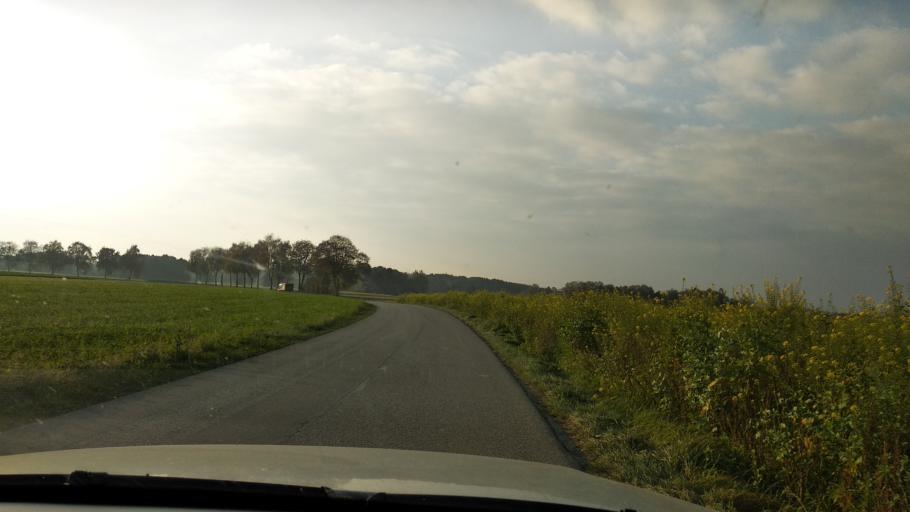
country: DE
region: Bavaria
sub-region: Upper Bavaria
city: Ottenhofen
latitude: 48.2202
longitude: 11.9056
